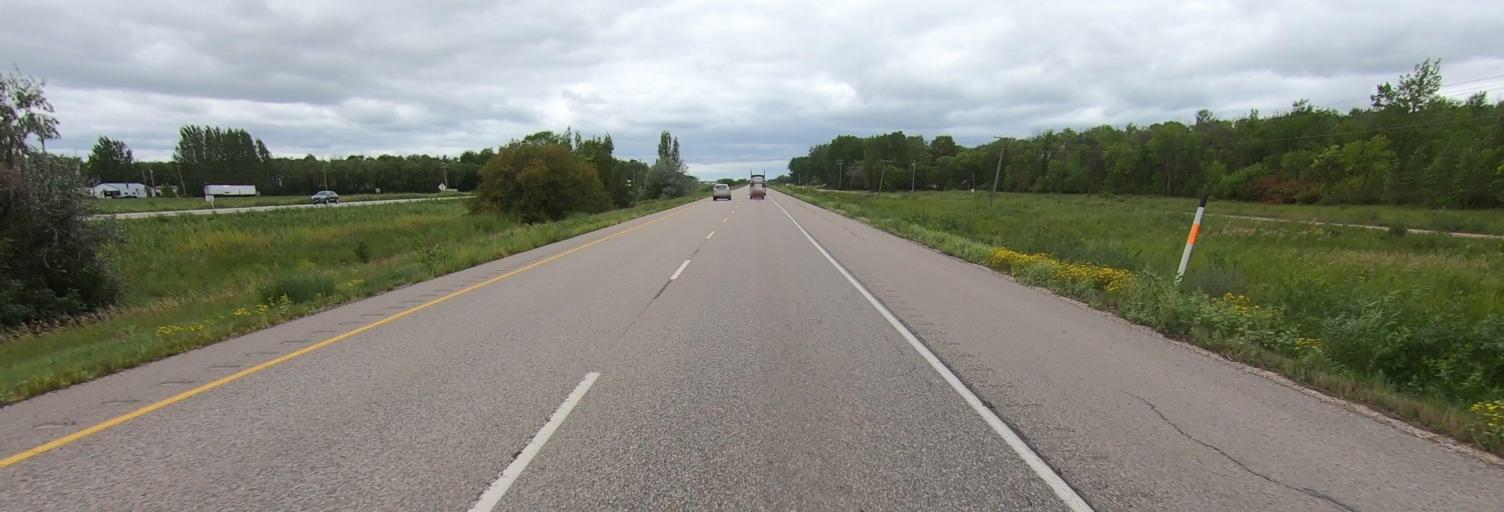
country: CA
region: Manitoba
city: Portage la Prairie
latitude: 49.9733
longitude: -98.1375
